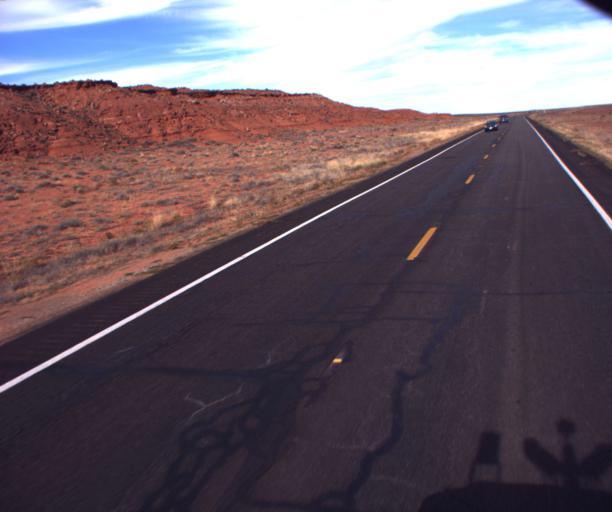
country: US
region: Arizona
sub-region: Navajo County
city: Kayenta
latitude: 36.9085
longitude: -109.7842
